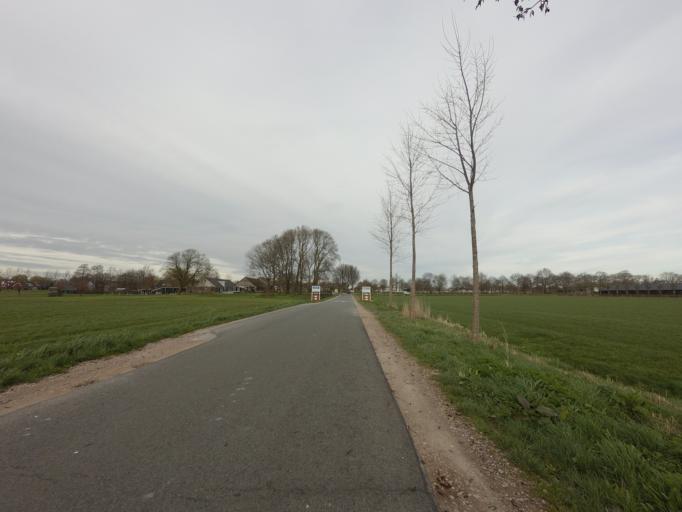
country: NL
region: Utrecht
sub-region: Gemeente De Ronde Venen
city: Mijdrecht
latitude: 52.1981
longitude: 4.8513
